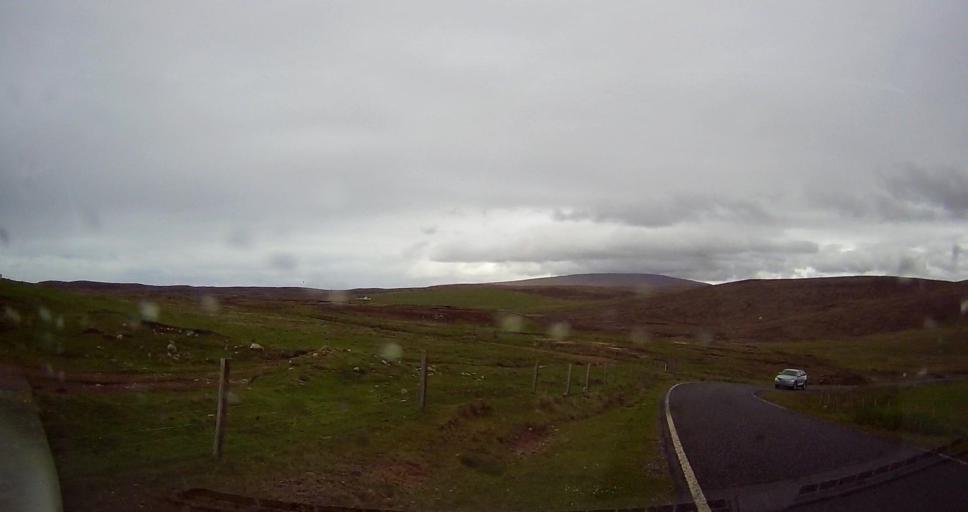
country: GB
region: Scotland
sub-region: Shetland Islands
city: Lerwick
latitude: 60.4942
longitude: -1.5571
